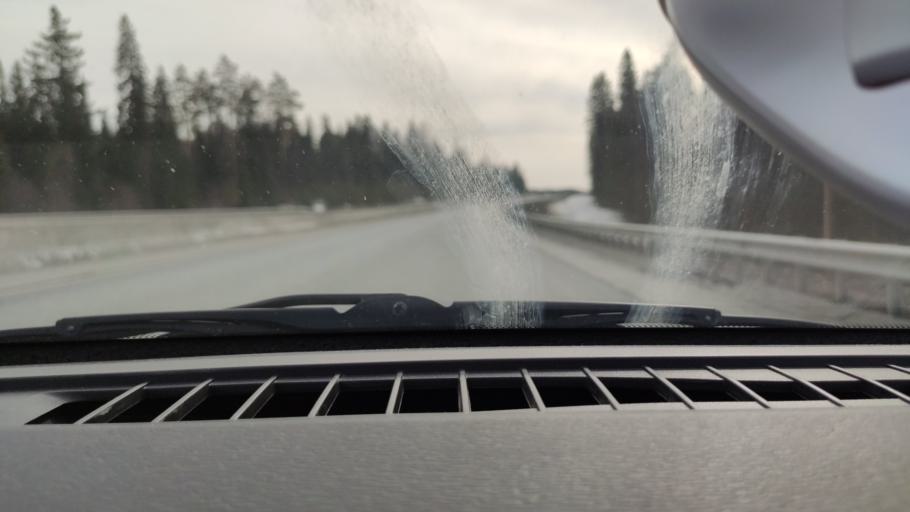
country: RU
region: Perm
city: Ferma
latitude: 57.9708
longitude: 56.4020
